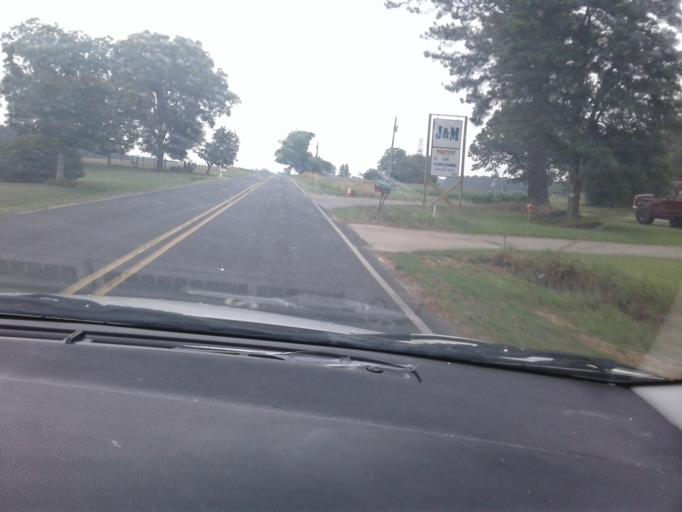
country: US
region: North Carolina
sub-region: Harnett County
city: Coats
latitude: 35.3763
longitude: -78.6497
